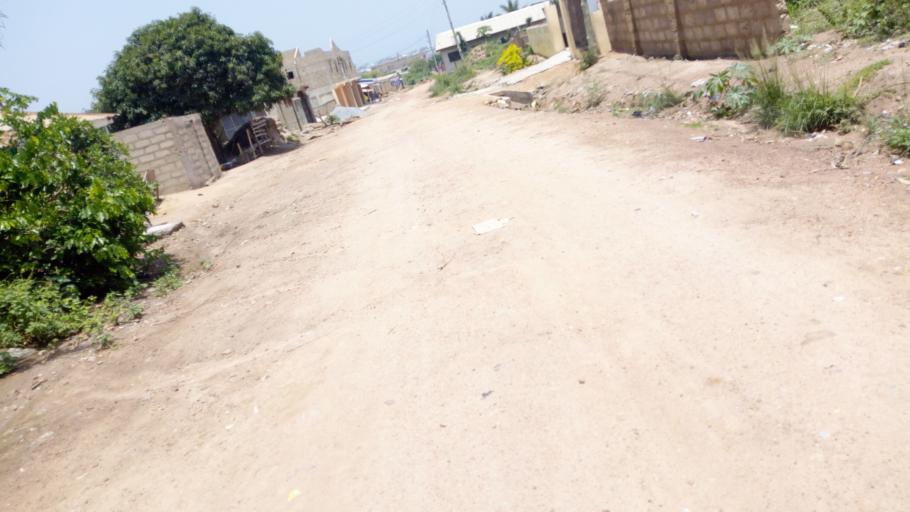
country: GH
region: Central
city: Kasoa
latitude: 5.5045
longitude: -0.4490
